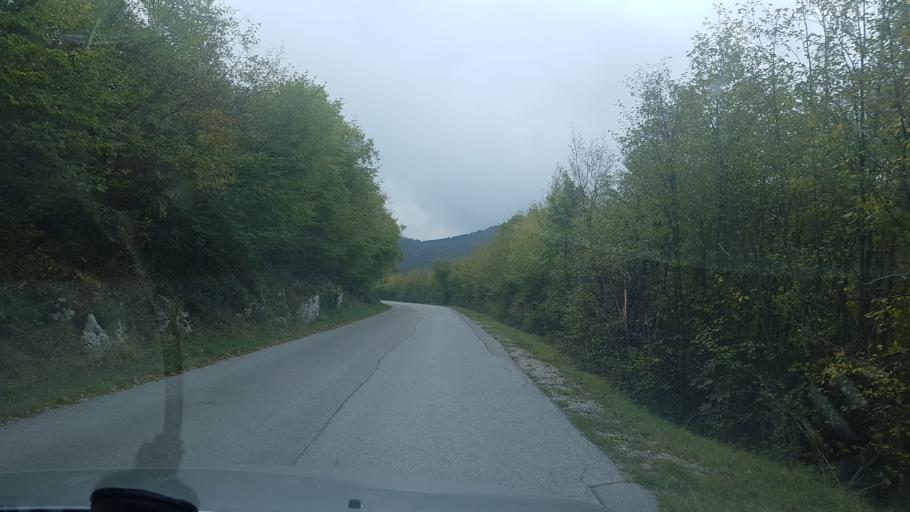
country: SI
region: Hrpelje-Kozina
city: Kozina
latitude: 45.5194
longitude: 13.9567
